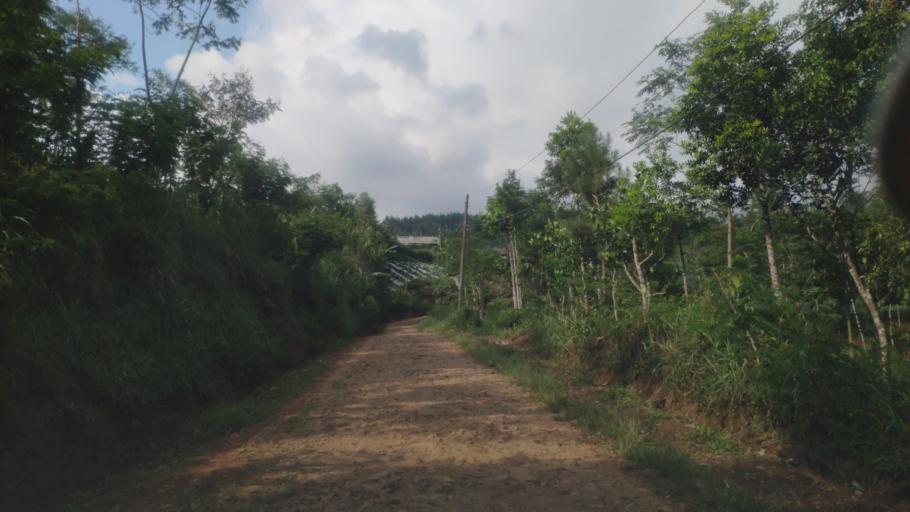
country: ID
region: Central Java
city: Buaran
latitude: -7.2400
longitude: 109.6836
